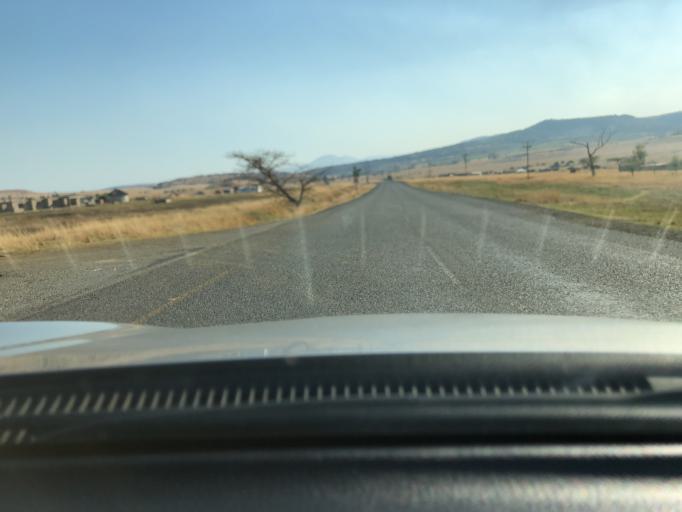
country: ZA
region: KwaZulu-Natal
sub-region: uThukela District Municipality
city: Ekuvukeni
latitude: -28.3333
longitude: 30.0528
